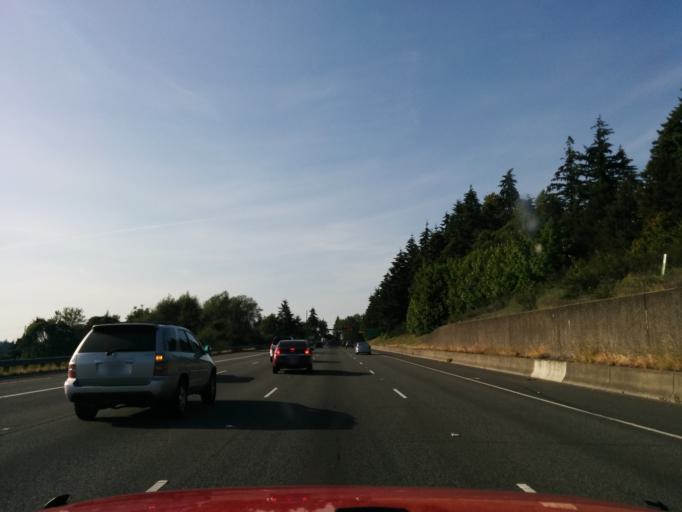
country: US
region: Washington
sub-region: King County
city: Newport
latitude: 47.5891
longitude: -122.1798
